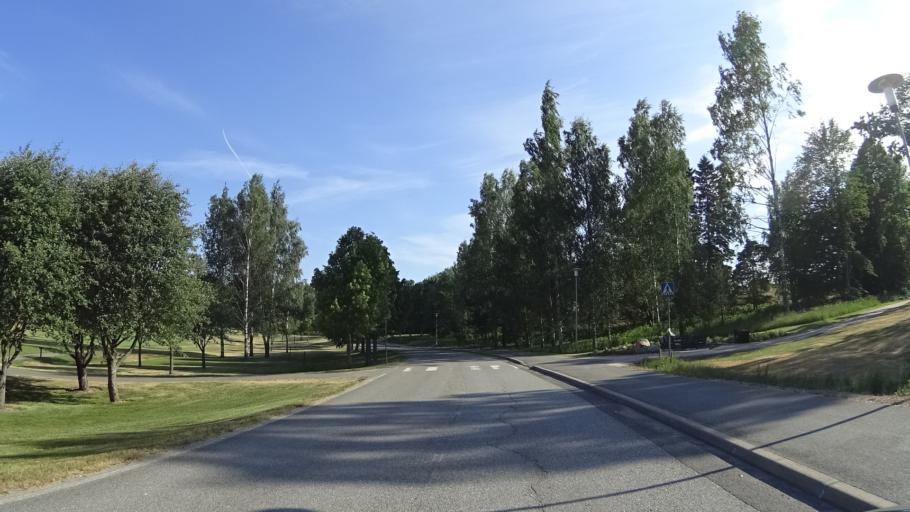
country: FI
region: Uusimaa
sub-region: Helsinki
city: Siuntio
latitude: 60.0755
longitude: 24.2850
